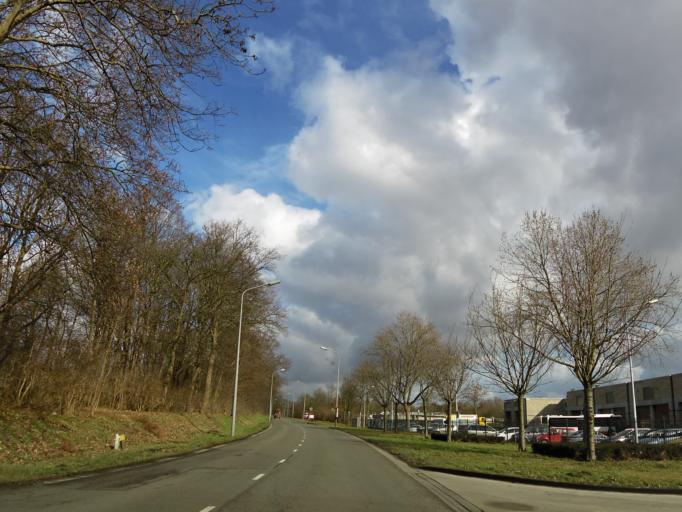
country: NL
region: Limburg
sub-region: Gemeente Maastricht
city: Maastricht
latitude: 50.8702
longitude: 5.7010
